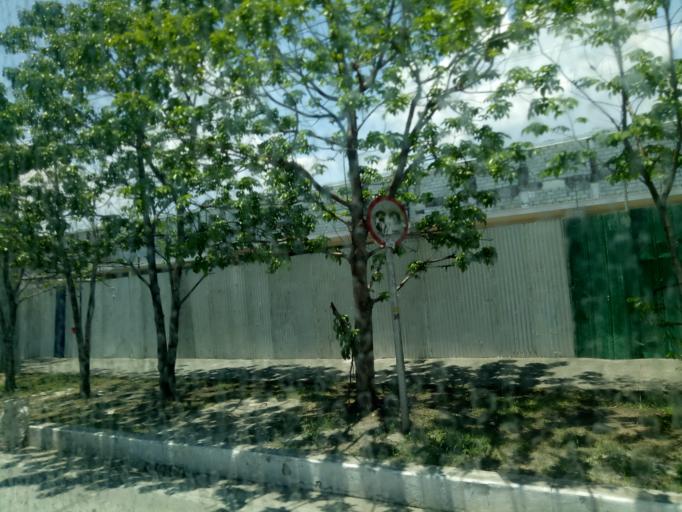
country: PH
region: Calabarzon
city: Bagong Pagasa
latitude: 14.7303
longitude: 121.0473
